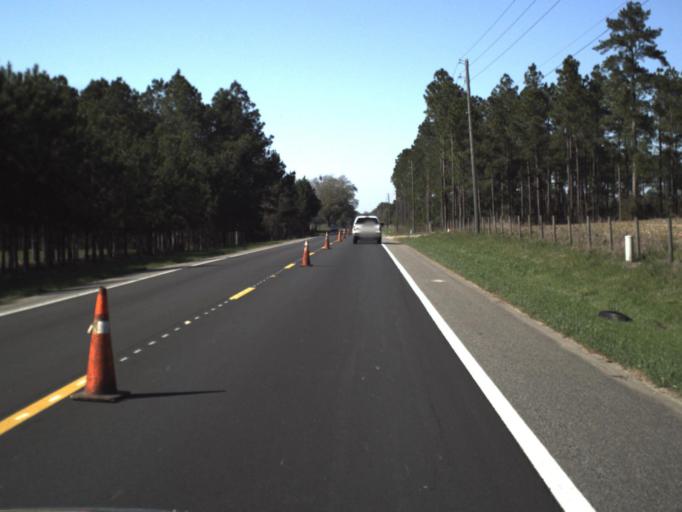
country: US
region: Florida
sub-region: Jackson County
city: Marianna
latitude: 30.6879
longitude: -85.1777
